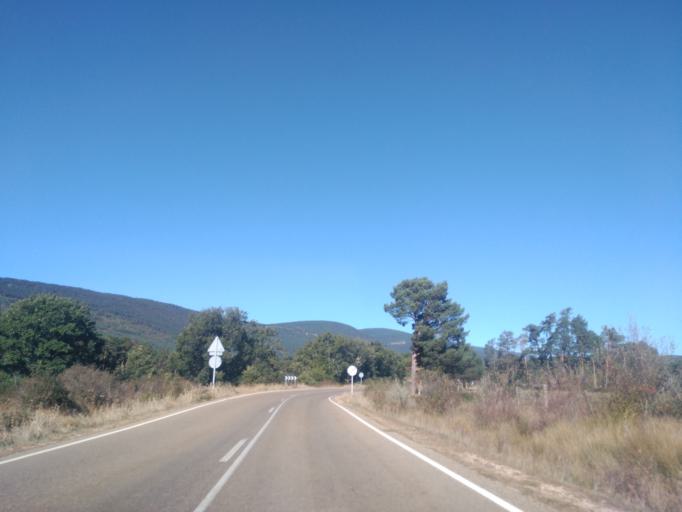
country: ES
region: Castille and Leon
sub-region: Provincia de Soria
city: Vinuesa
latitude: 41.9207
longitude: -2.7596
